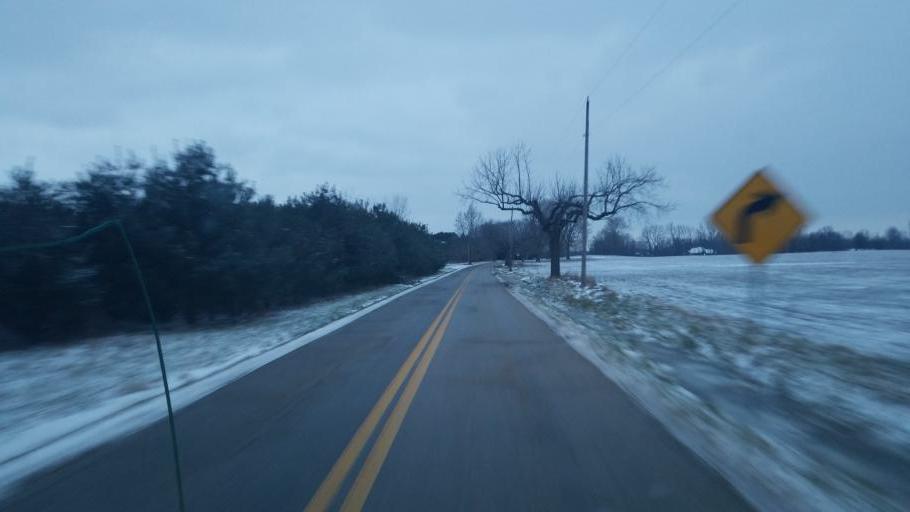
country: US
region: Ohio
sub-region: Delaware County
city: Sunbury
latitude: 40.2122
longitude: -82.8586
